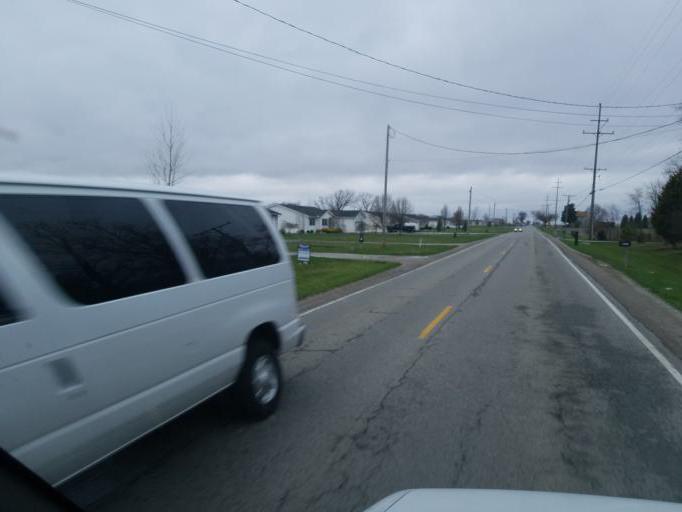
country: US
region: Ohio
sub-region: Marion County
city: Marion
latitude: 40.6367
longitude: -83.0732
